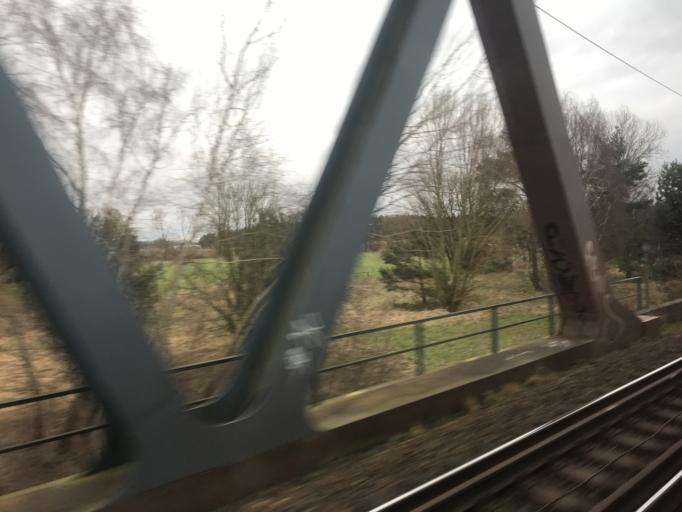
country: DE
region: Lower Saxony
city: Meinersen
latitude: 52.4548
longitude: 10.3509
